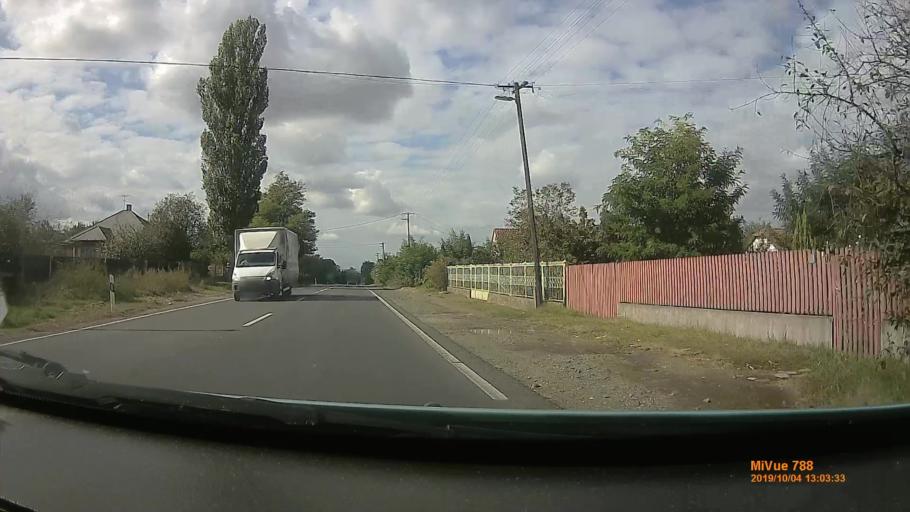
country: HU
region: Szabolcs-Szatmar-Bereg
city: Nyirtelek
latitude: 47.9583
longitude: 21.6323
